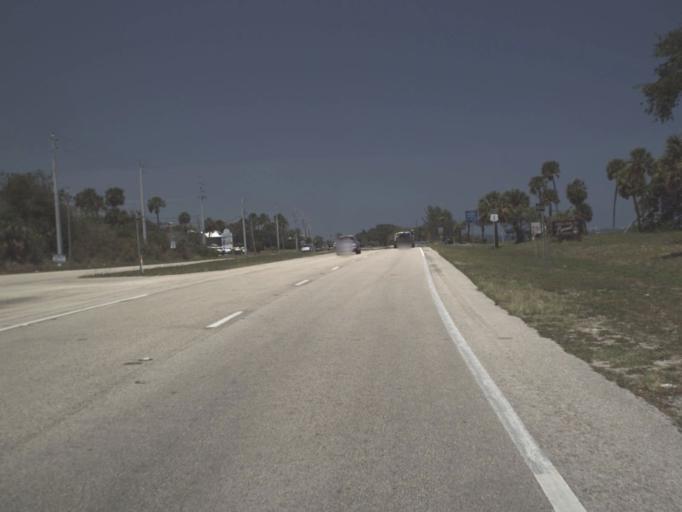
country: US
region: Florida
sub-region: Indian River County
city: Roseland
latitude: 27.8576
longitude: -80.4919
